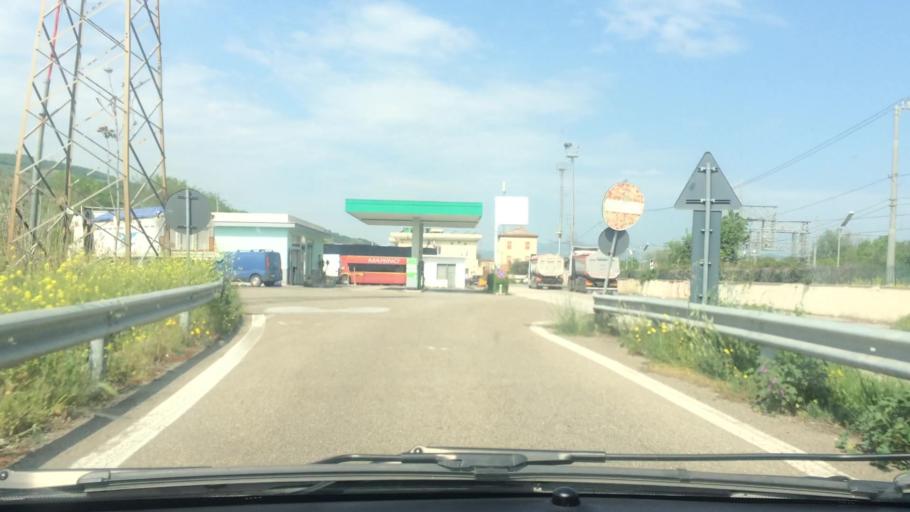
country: IT
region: Basilicate
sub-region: Provincia di Matera
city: Grottole
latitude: 40.5828
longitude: 16.3538
